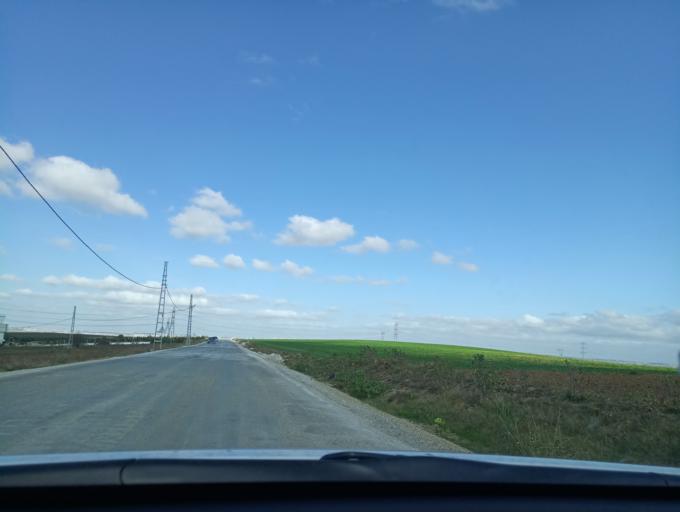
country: TR
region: Tekirdag
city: Corlu
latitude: 41.0528
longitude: 27.8352
